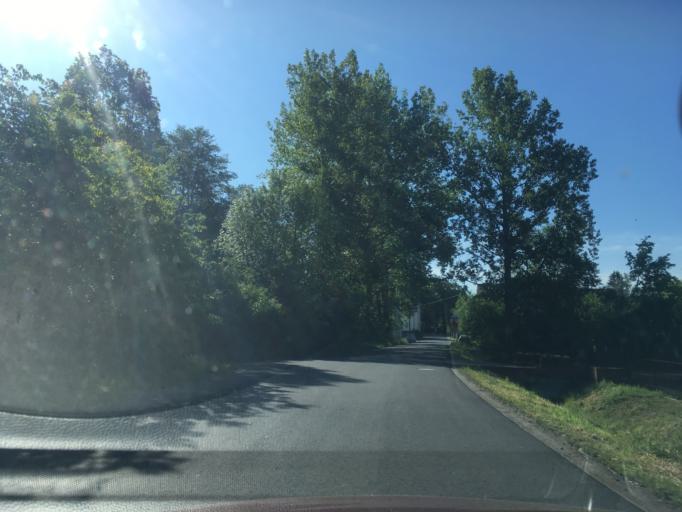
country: PL
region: Lower Silesian Voivodeship
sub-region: Powiat zgorzelecki
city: Sulikow
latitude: 51.0926
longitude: 15.0483
